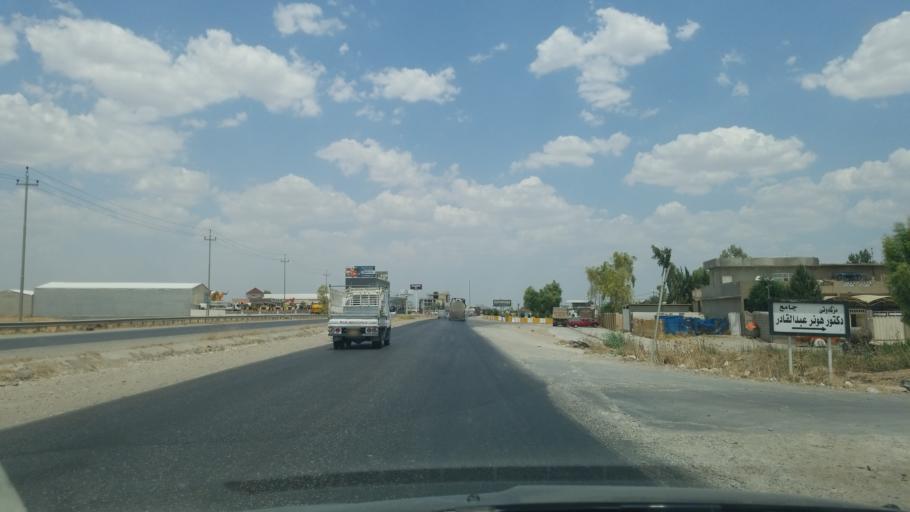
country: IQ
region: Arbil
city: Erbil
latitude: 36.0977
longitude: 44.0214
